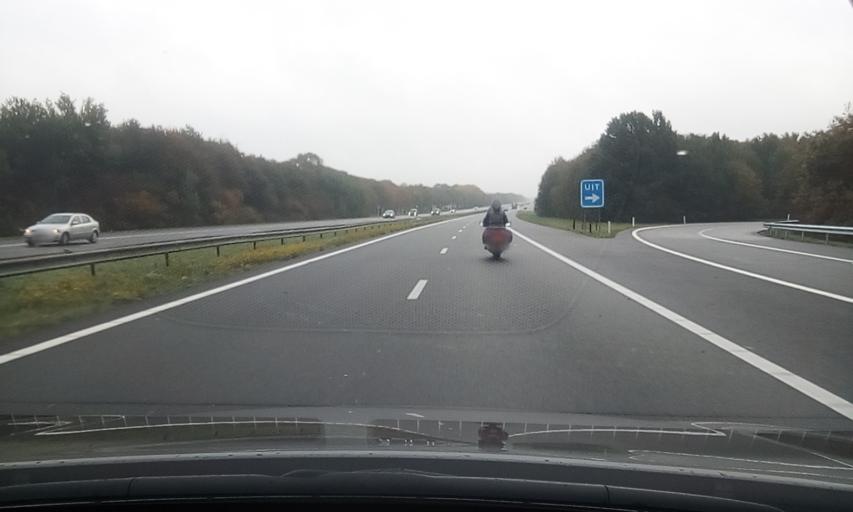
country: NL
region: Overijssel
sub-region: Gemeente Staphorst
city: Staphorst
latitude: 52.6842
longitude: 6.2712
